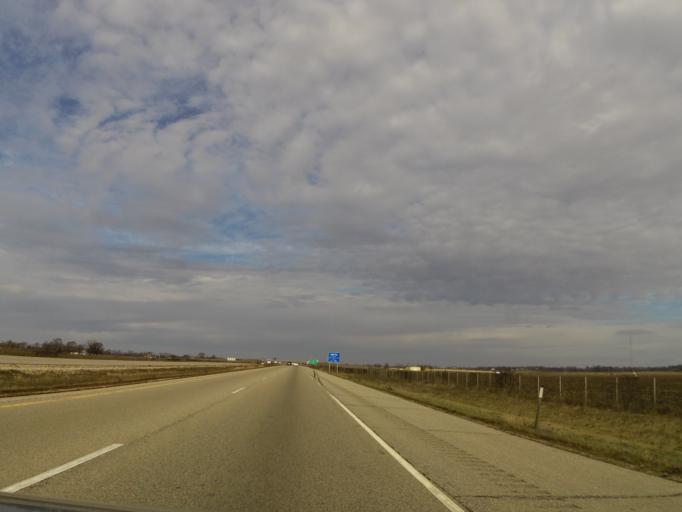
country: US
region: Wisconsin
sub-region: Rock County
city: Beloit
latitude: 42.5405
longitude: -88.9749
